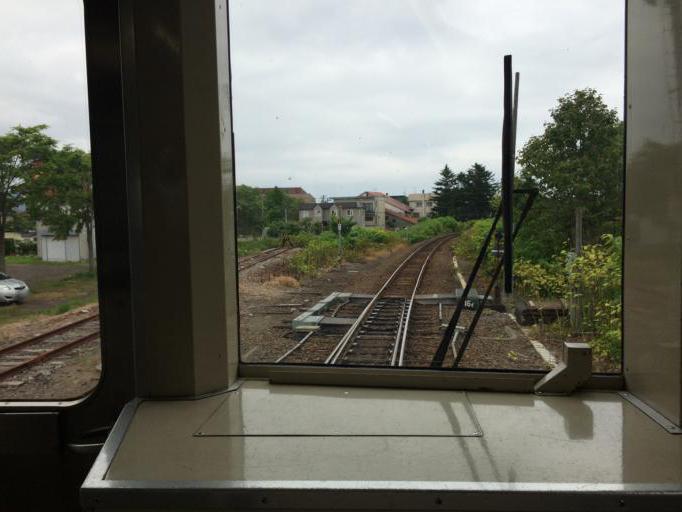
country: JP
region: Hokkaido
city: Yoichi
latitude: 43.1891
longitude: 140.7953
